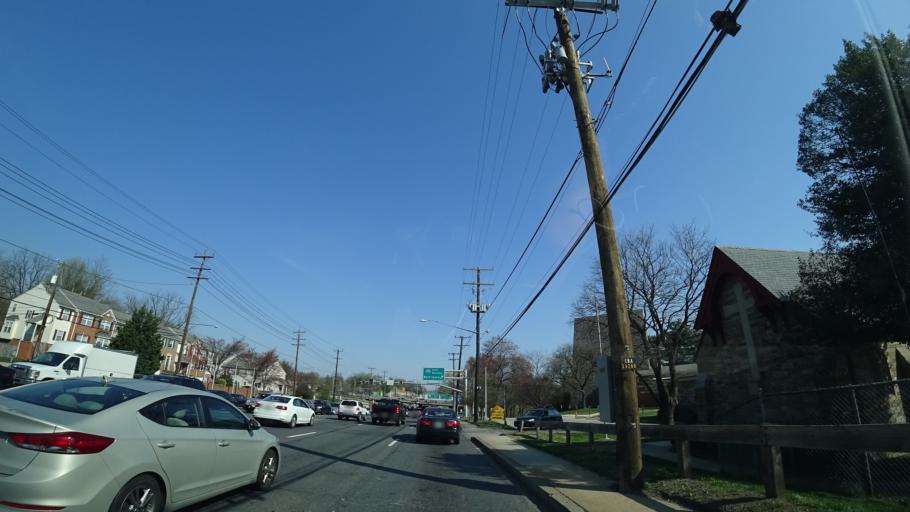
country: US
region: Maryland
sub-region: Montgomery County
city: Forest Glen
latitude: 39.0115
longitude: -77.0411
